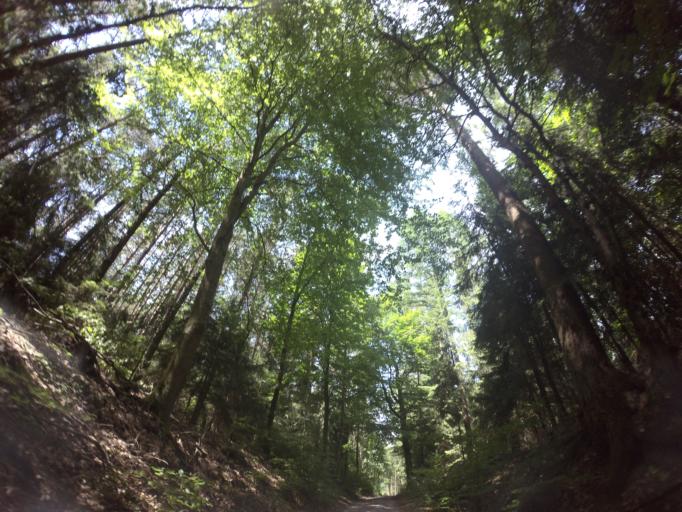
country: PL
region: West Pomeranian Voivodeship
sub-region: Powiat choszczenski
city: Recz
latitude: 53.3278
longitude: 15.5273
